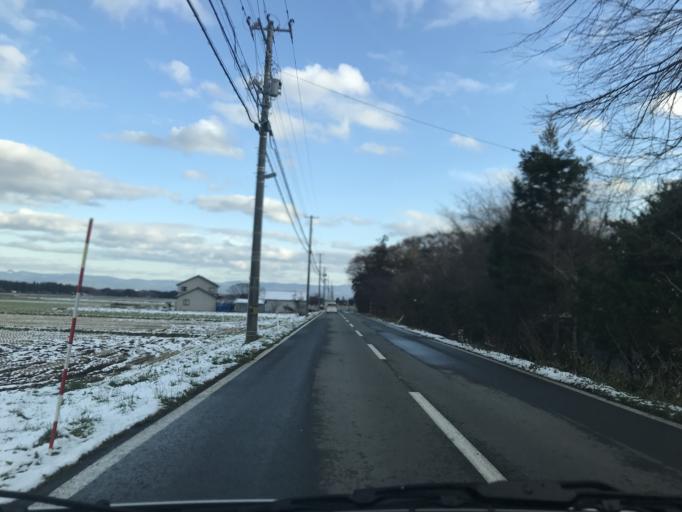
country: JP
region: Iwate
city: Kitakami
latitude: 39.2112
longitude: 141.0327
